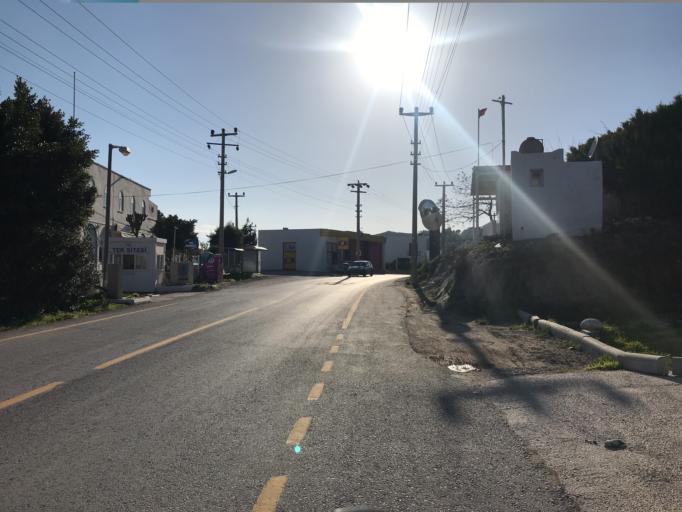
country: TR
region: Mugla
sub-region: Bodrum
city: Turgutreis
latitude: 36.9761
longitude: 27.3029
